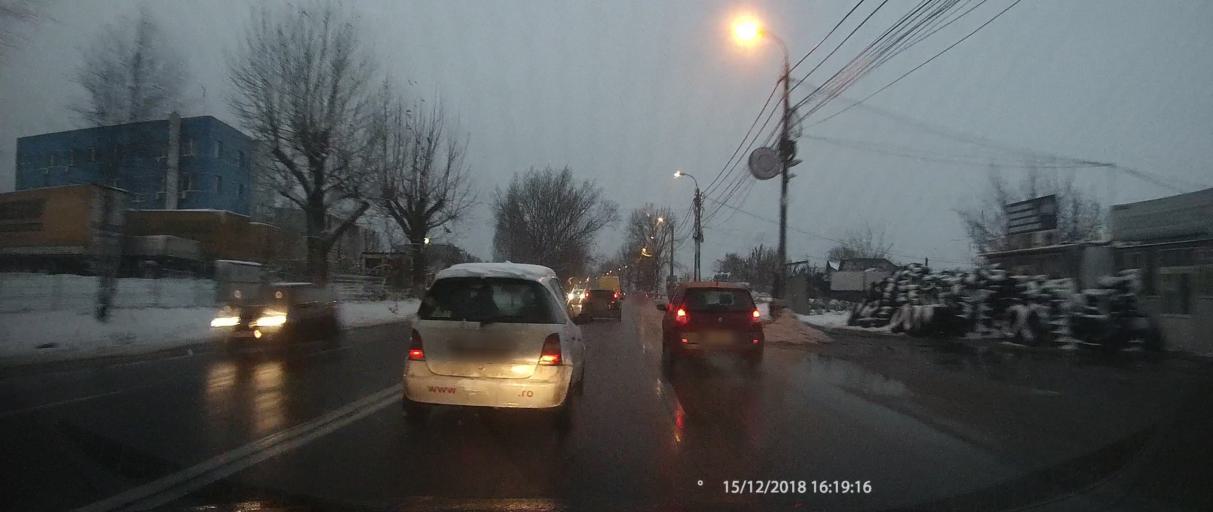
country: RO
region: Galati
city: Galati
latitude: 45.4239
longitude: 28.0049
